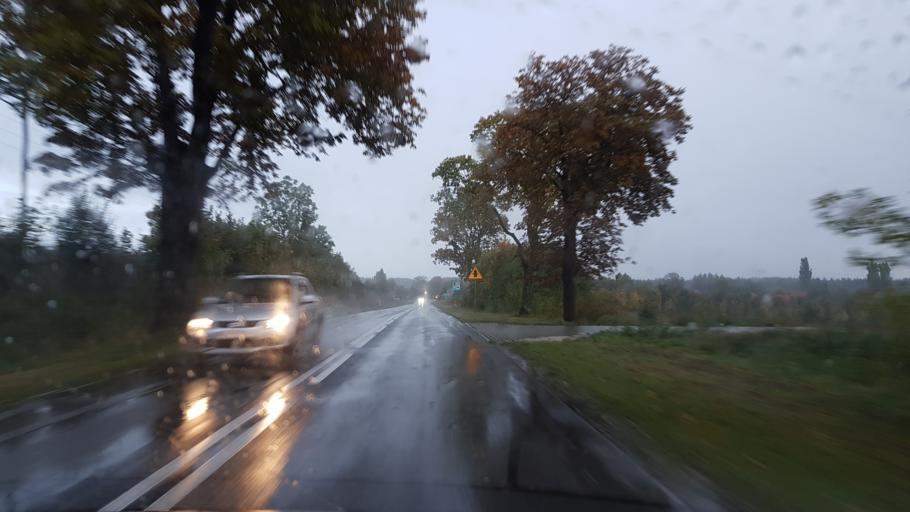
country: PL
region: Greater Poland Voivodeship
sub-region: Powiat pilski
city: Szydlowo
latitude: 53.1585
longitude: 16.6522
